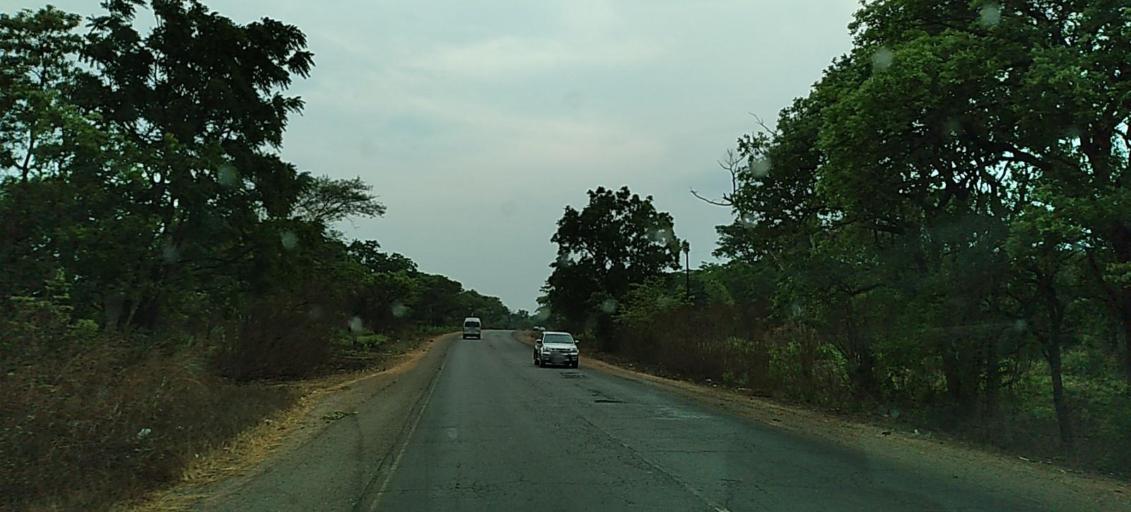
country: ZM
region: Copperbelt
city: Luanshya
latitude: -13.0789
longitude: 28.4463
